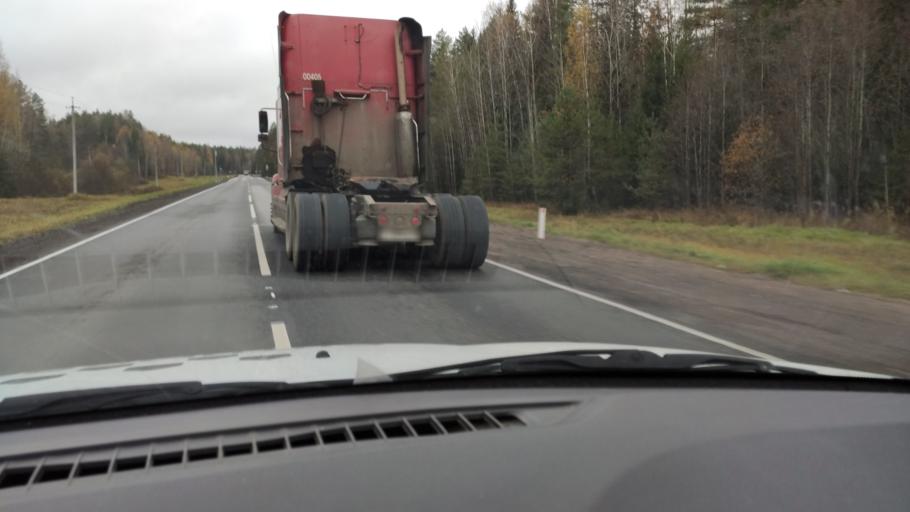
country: RU
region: Kirov
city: Belaya Kholunitsa
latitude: 58.8314
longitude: 50.6845
